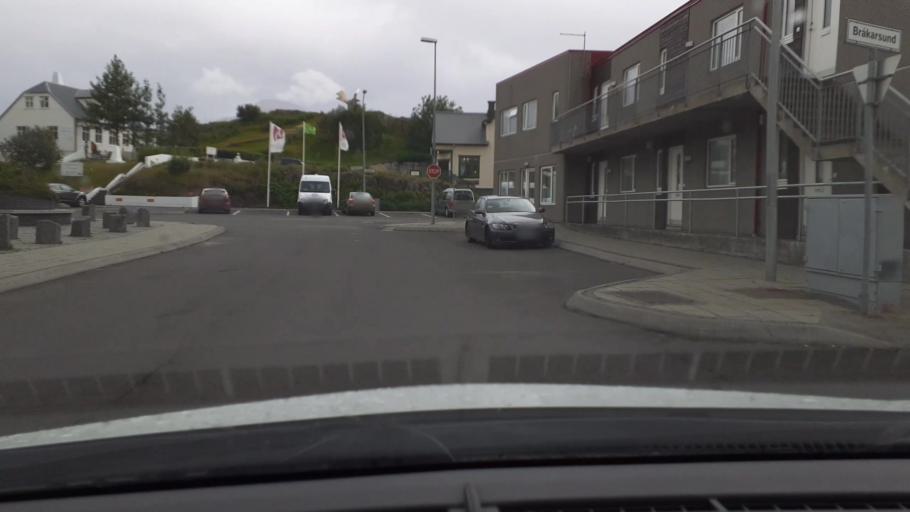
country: IS
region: West
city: Borgarnes
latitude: 64.5363
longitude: -21.9240
